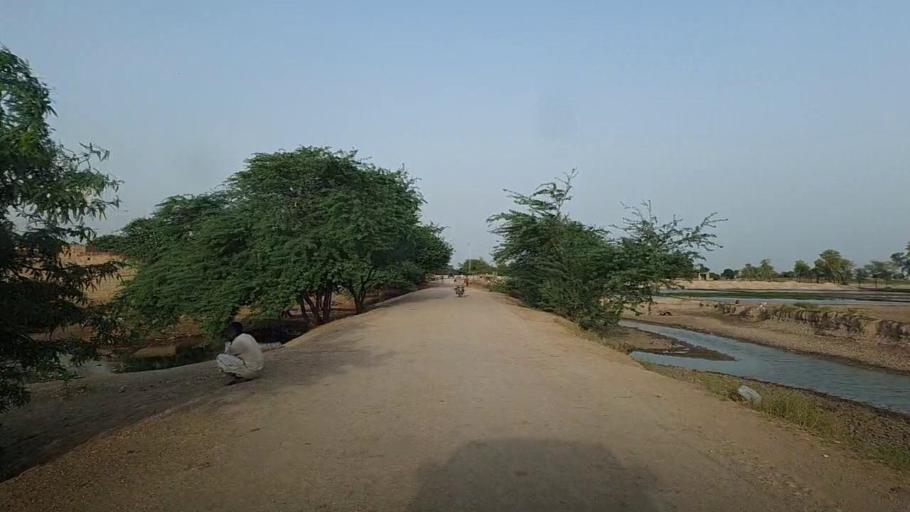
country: PK
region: Sindh
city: Mehar
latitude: 27.1635
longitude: 67.7898
